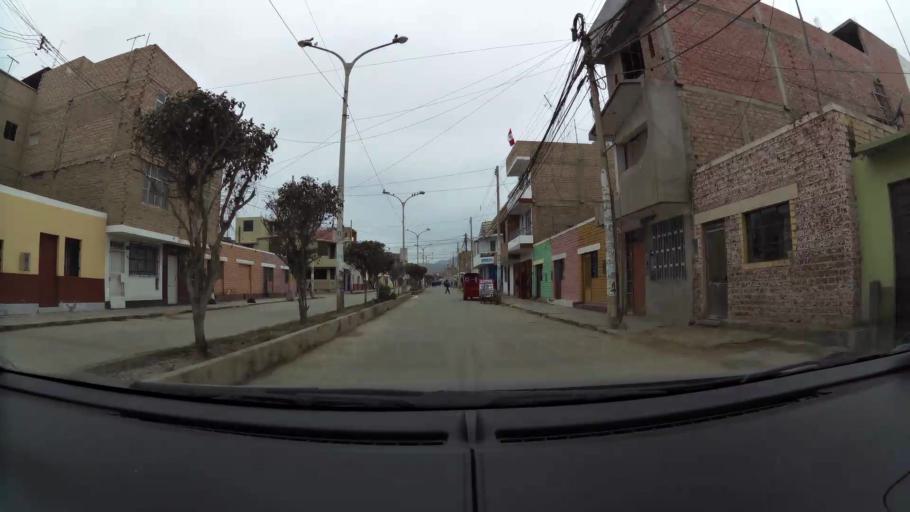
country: PE
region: Lima
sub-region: Barranca
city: Paramonga
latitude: -10.6737
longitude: -77.8172
